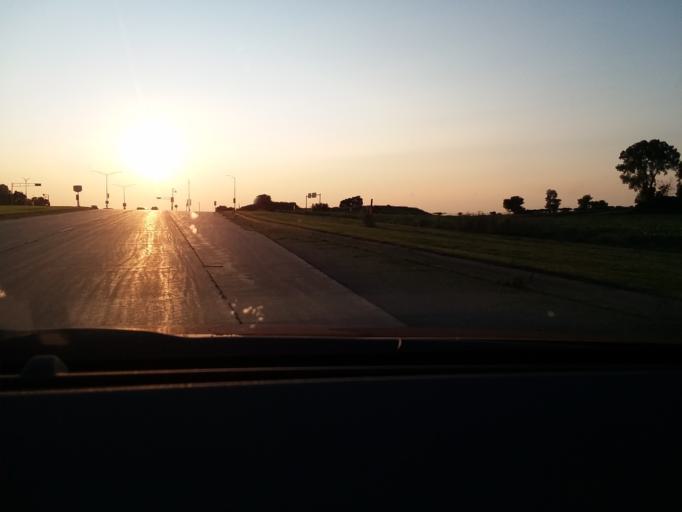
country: US
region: Wisconsin
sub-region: Dane County
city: Sun Prairie
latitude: 43.1441
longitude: -89.2806
